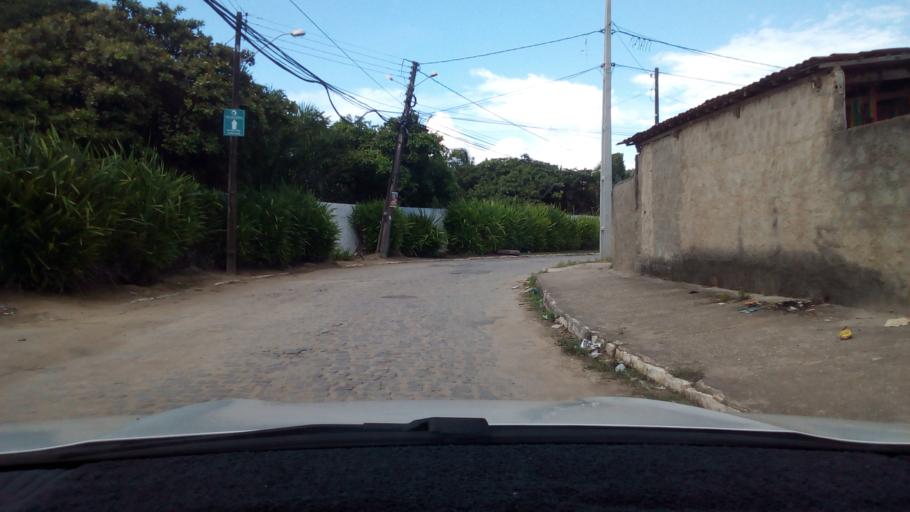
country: BR
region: Paraiba
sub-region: Joao Pessoa
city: Joao Pessoa
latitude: -7.1634
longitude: -34.8536
